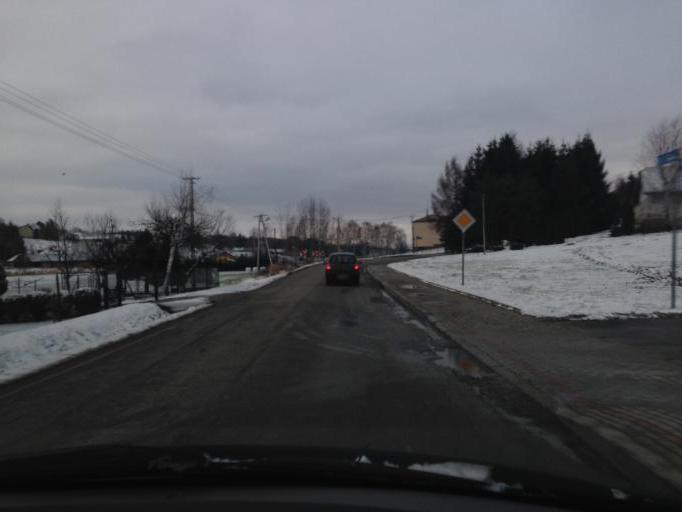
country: PL
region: Lesser Poland Voivodeship
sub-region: Powiat gorlicki
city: Moszczenica
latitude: 49.7230
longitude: 21.1069
